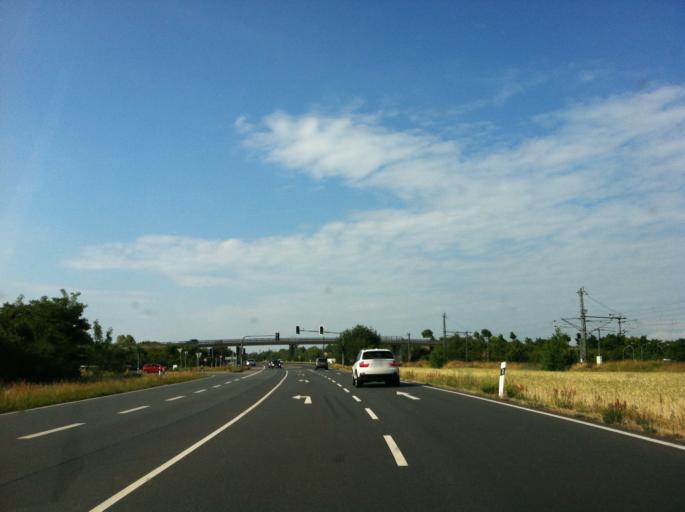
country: DE
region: Hesse
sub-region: Regierungsbezirk Darmstadt
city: Darmstadt
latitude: 49.9036
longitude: 8.6429
